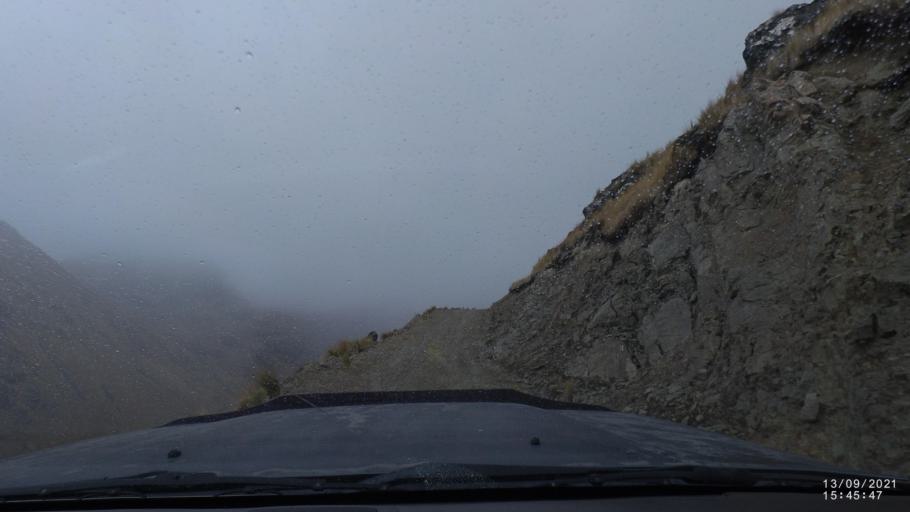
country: BO
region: Cochabamba
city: Colomi
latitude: -17.3169
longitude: -65.7220
